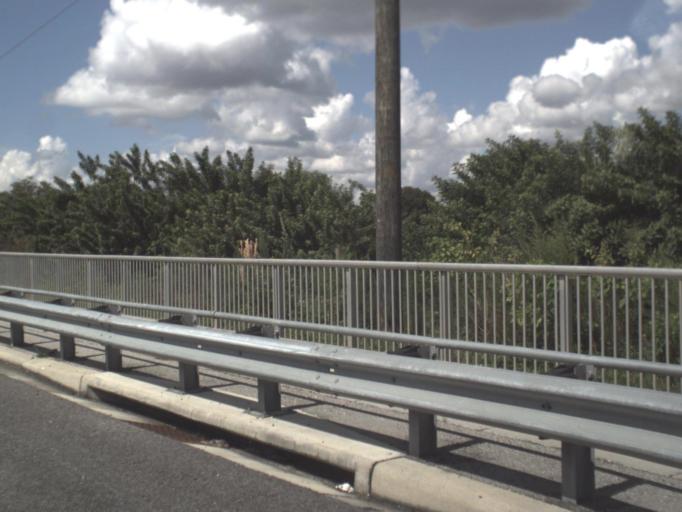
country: US
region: Florida
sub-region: Lee County
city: Tice
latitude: 26.6294
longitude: -81.7845
